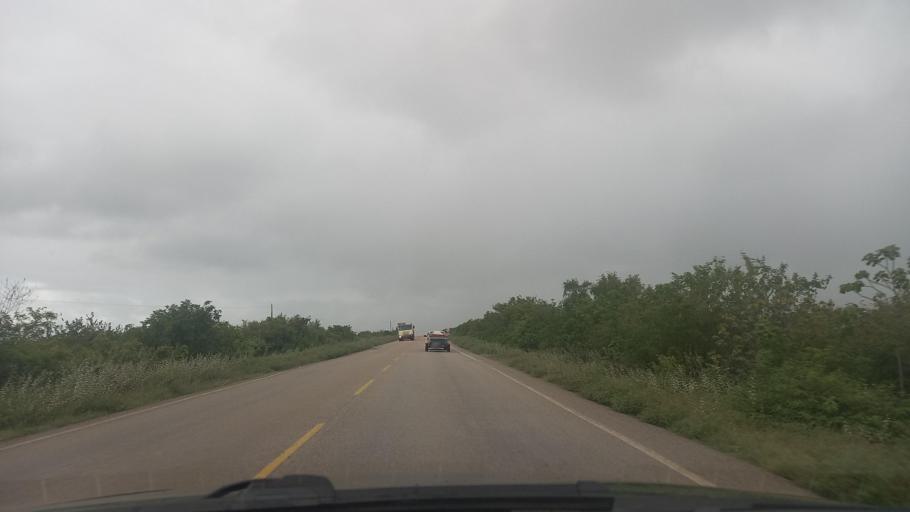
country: BR
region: Bahia
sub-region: Paulo Afonso
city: Paulo Afonso
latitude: -9.3373
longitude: -38.2840
